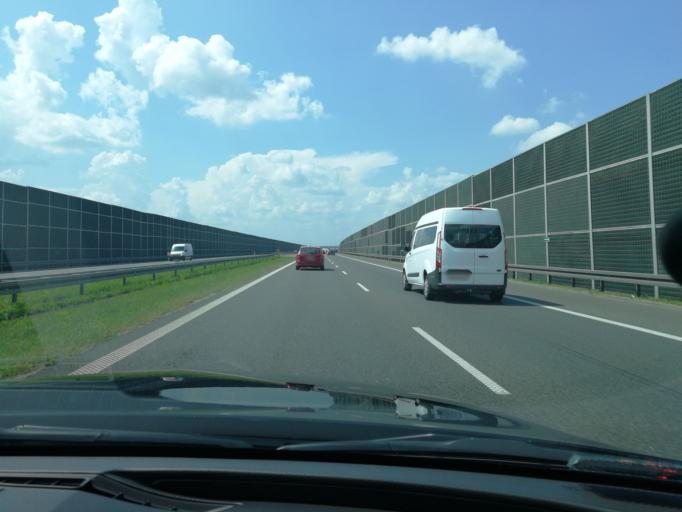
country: PL
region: Masovian Voivodeship
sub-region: Powiat pruszkowski
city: Brwinow
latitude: 52.1700
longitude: 20.7490
